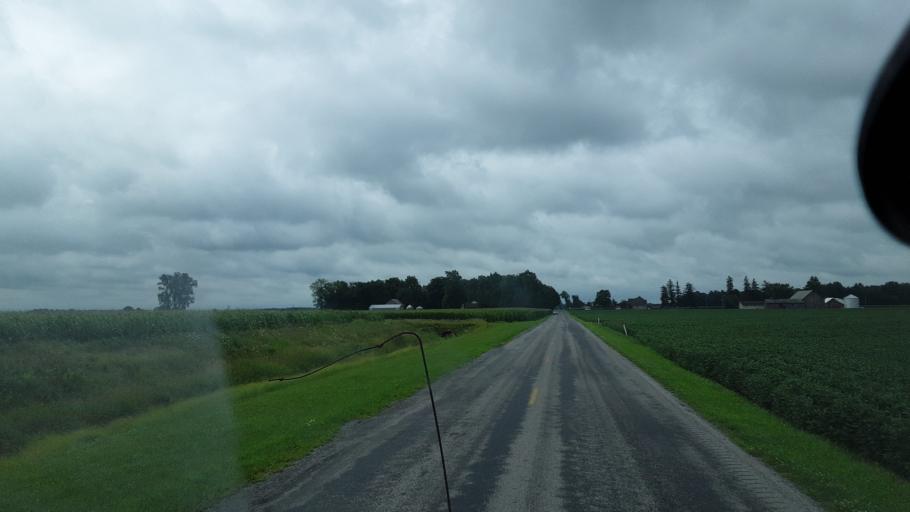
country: US
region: Indiana
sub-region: Wells County
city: Ossian
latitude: 40.8641
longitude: -85.1093
